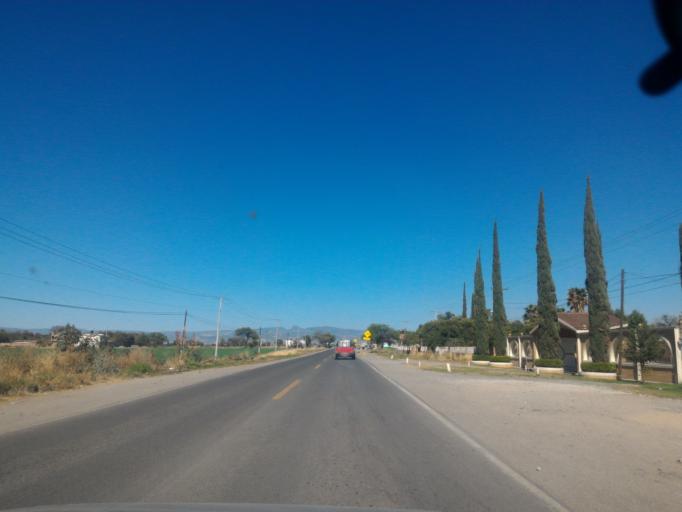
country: MX
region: Guanajuato
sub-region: Leon
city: Malagana (San Antonio del Monte)
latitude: 21.0480
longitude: -101.7552
